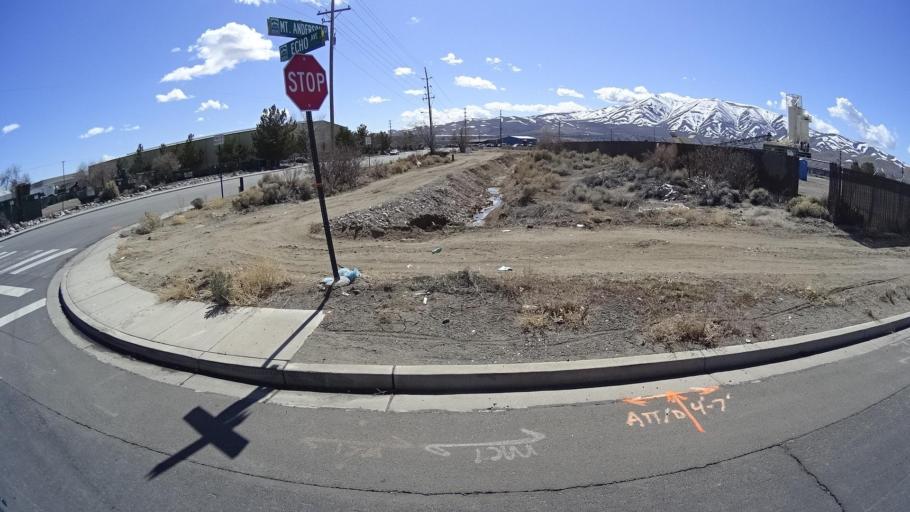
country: US
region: Nevada
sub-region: Washoe County
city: Lemmon Valley
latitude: 39.6547
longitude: -119.8869
